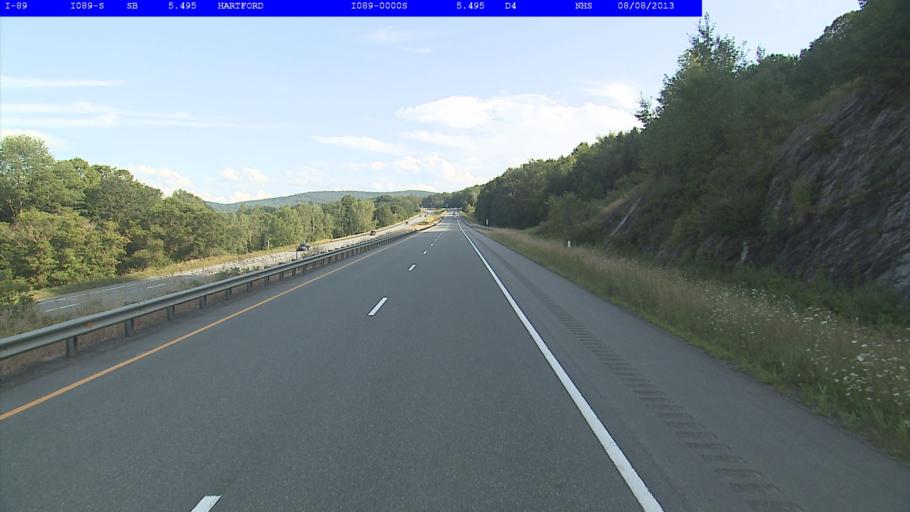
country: US
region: Vermont
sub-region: Windsor County
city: White River Junction
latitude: 43.6852
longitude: -72.4025
